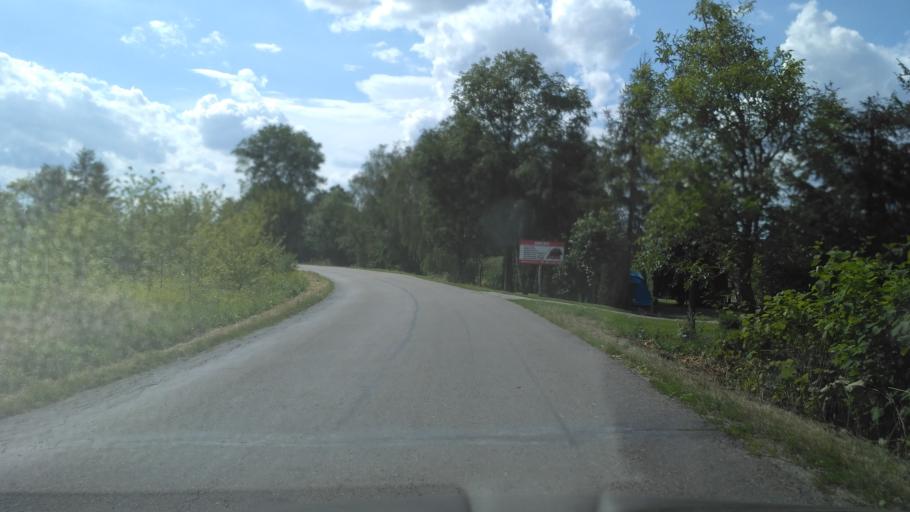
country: PL
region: Lublin Voivodeship
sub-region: Powiat leczynski
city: Milejow
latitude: 51.2176
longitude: 22.8999
